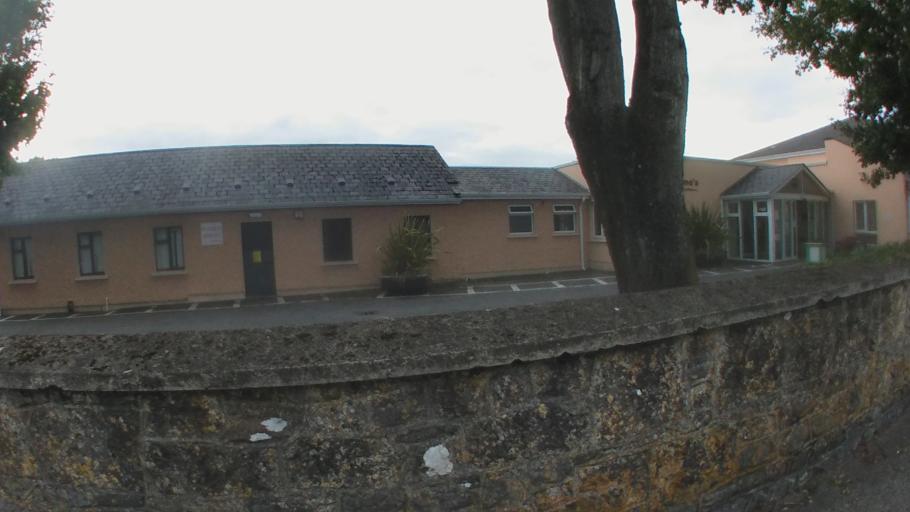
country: IE
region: Leinster
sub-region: County Carlow
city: Carlow
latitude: 52.8398
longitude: -6.9228
